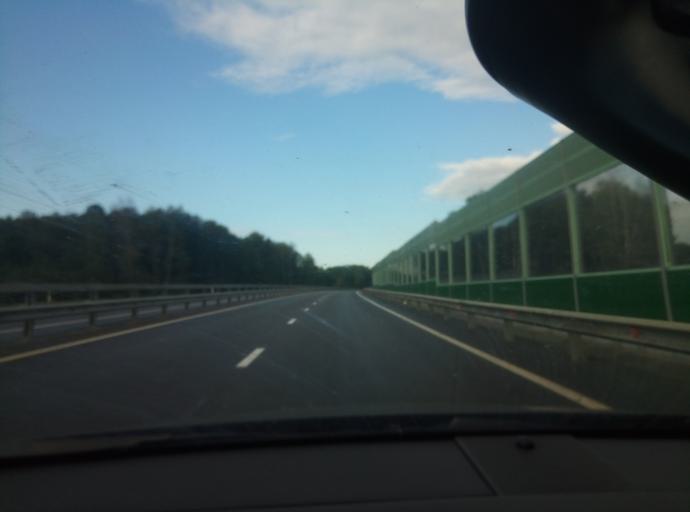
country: RU
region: Kaluga
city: Kaluga
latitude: 54.4448
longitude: 36.2357
